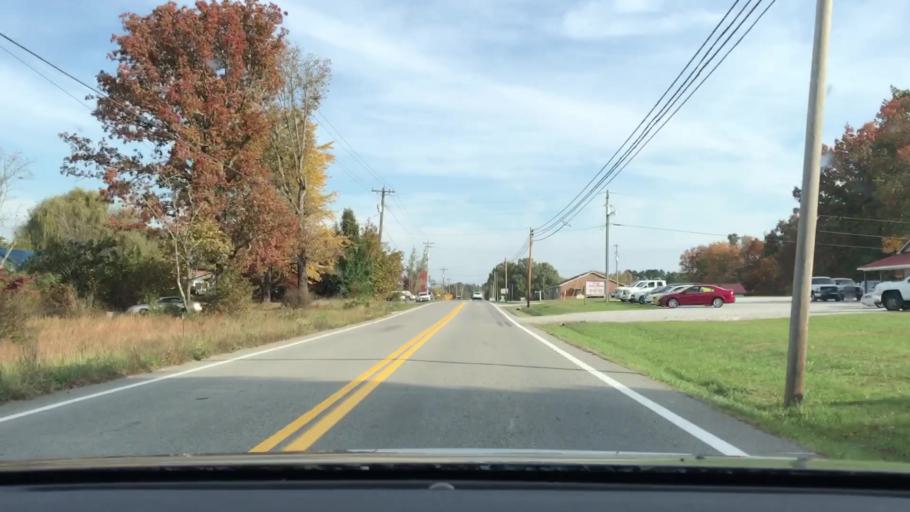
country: US
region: Tennessee
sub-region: Fentress County
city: Grimsley
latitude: 36.2271
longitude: -85.0094
